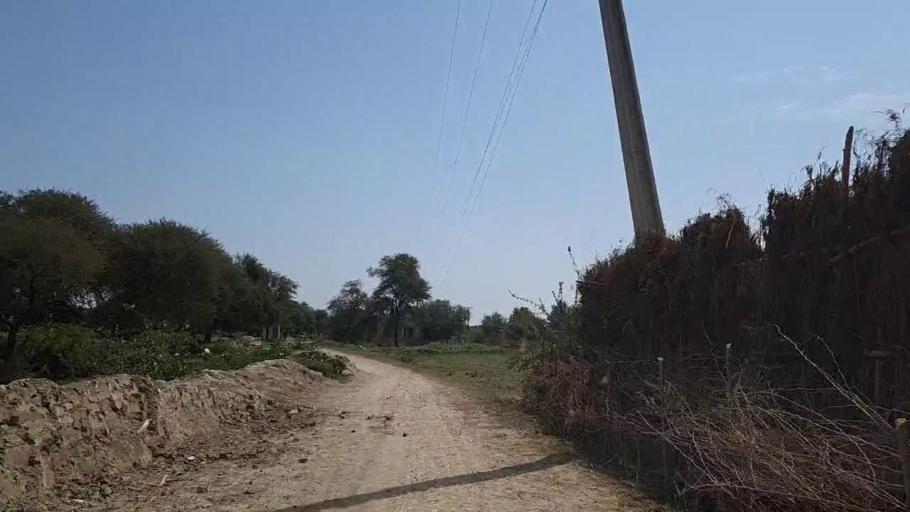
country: PK
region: Sindh
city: Mirpur Batoro
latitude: 24.7737
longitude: 68.2473
